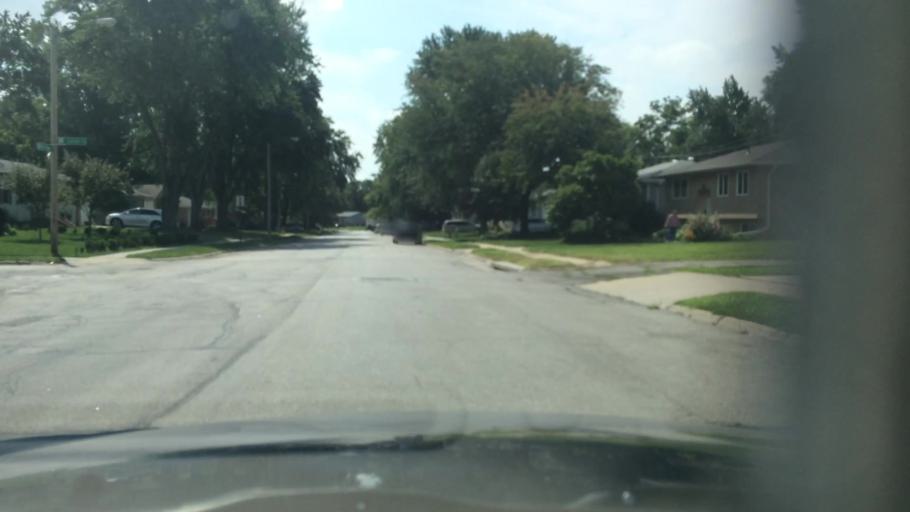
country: US
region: Nebraska
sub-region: Sarpy County
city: La Vista
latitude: 41.1834
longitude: -96.0355
